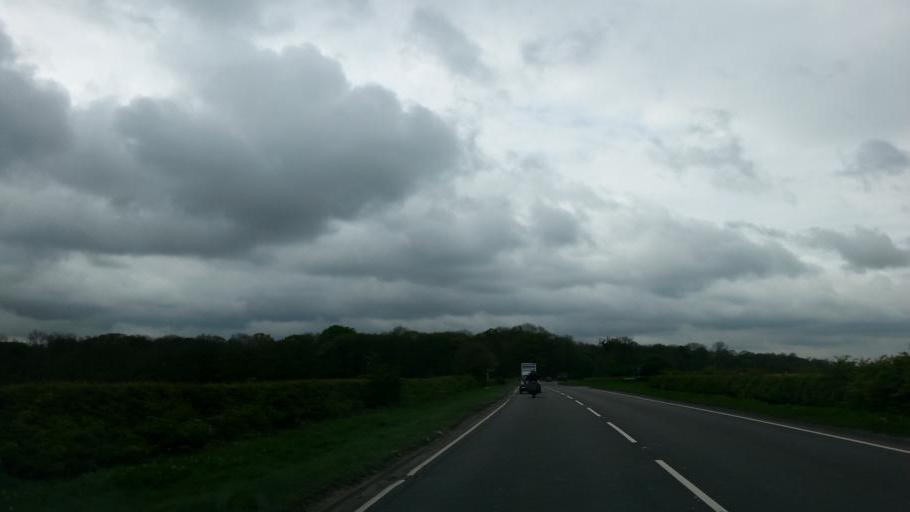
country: GB
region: England
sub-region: Leicestershire
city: Lutterworth
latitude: 52.4182
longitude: -1.2309
